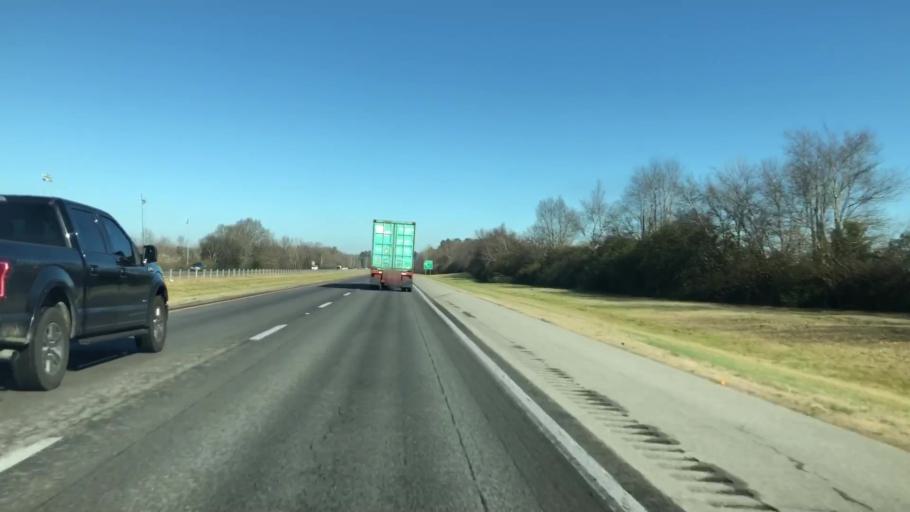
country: US
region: Alabama
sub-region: Limestone County
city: Athens
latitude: 34.8131
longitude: -86.9386
